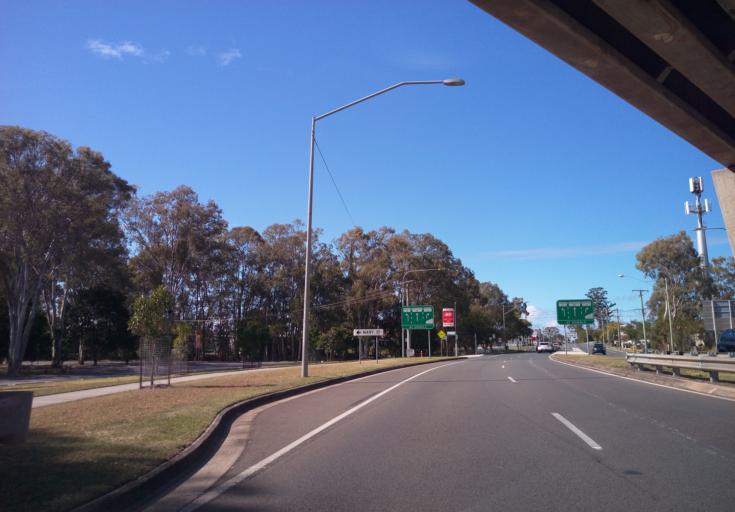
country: AU
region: Queensland
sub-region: Redland
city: Wellington Point
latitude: -27.4933
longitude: 153.2146
